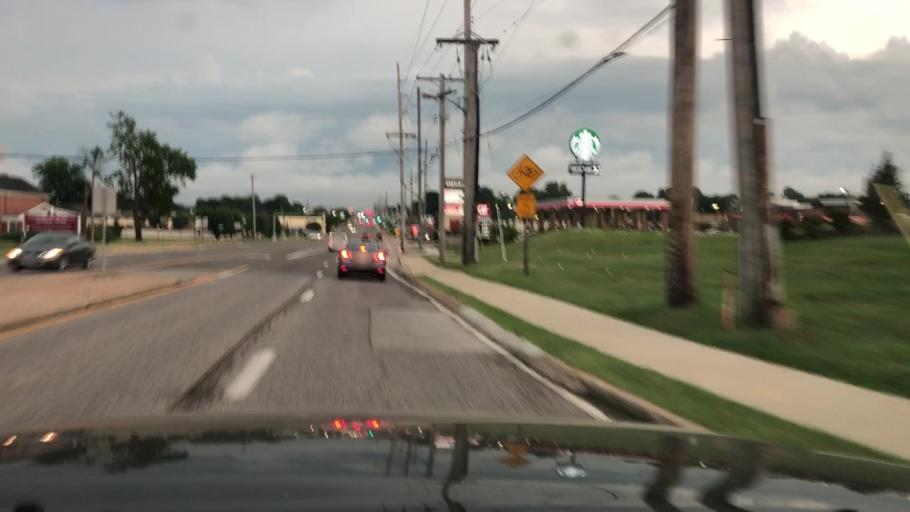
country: US
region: Missouri
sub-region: Saint Louis County
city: Saint Ann
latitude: 38.7372
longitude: -90.3983
